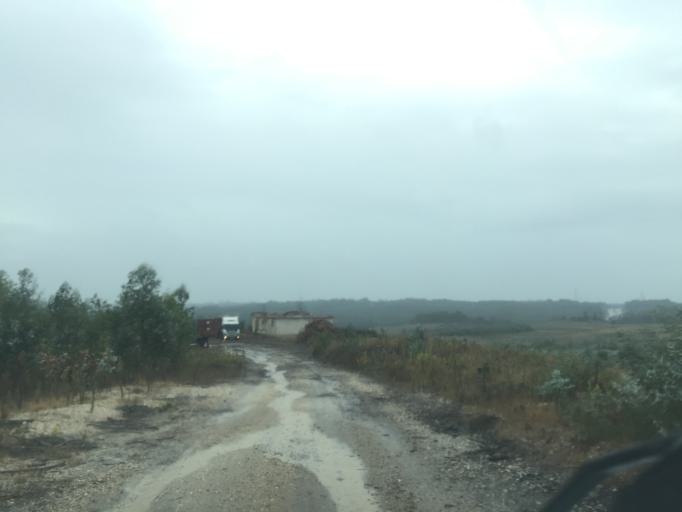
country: PT
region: Coimbra
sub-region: Figueira da Foz
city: Lavos
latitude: 40.0750
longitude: -8.7874
